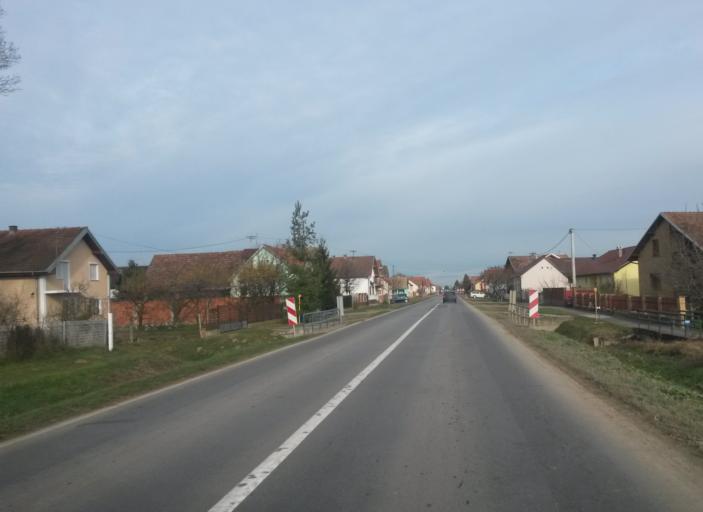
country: HR
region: Osjecko-Baranjska
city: Vuka
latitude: 45.4016
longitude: 18.4630
